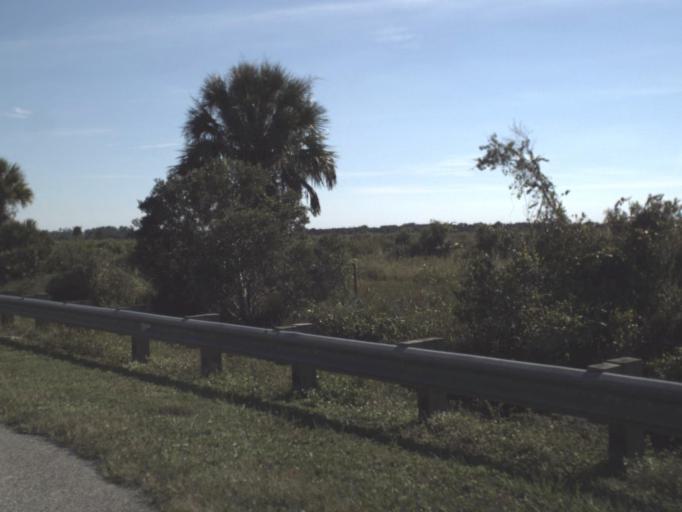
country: US
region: Florida
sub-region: Glades County
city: Moore Haven
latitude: 26.8793
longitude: -81.2266
